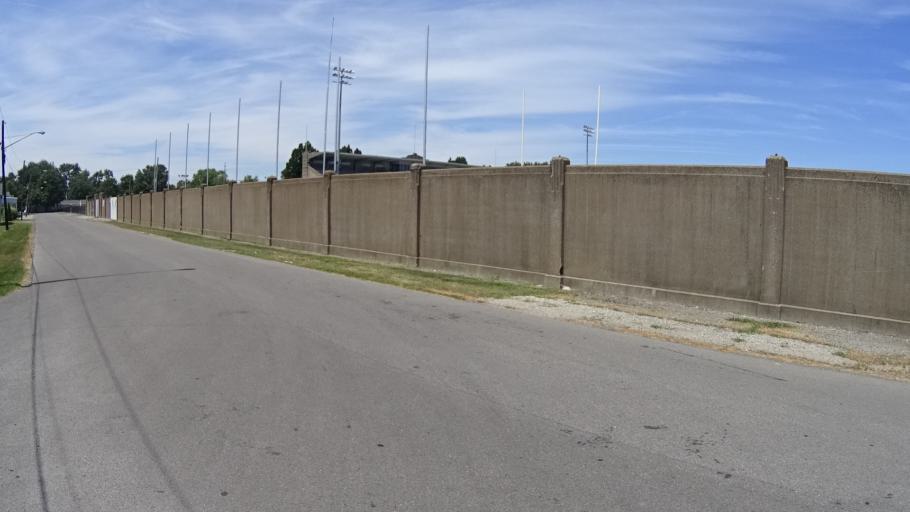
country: US
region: Ohio
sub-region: Erie County
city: Sandusky
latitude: 41.4340
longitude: -82.7168
